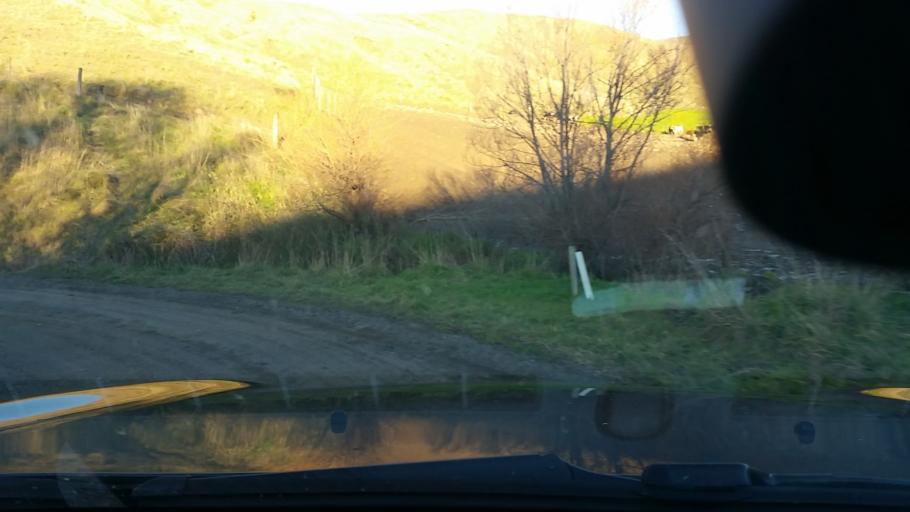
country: NZ
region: Marlborough
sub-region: Marlborough District
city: Blenheim
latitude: -41.7502
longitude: 174.0676
